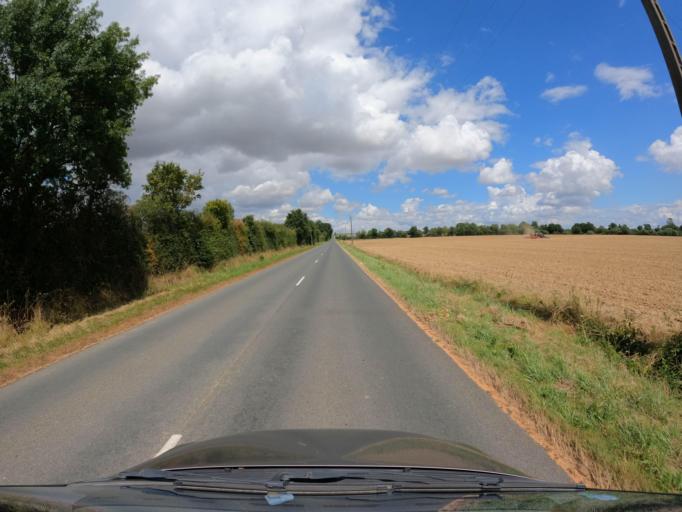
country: FR
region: Pays de la Loire
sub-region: Departement de Maine-et-Loire
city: Mire
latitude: 47.7394
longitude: -0.5089
